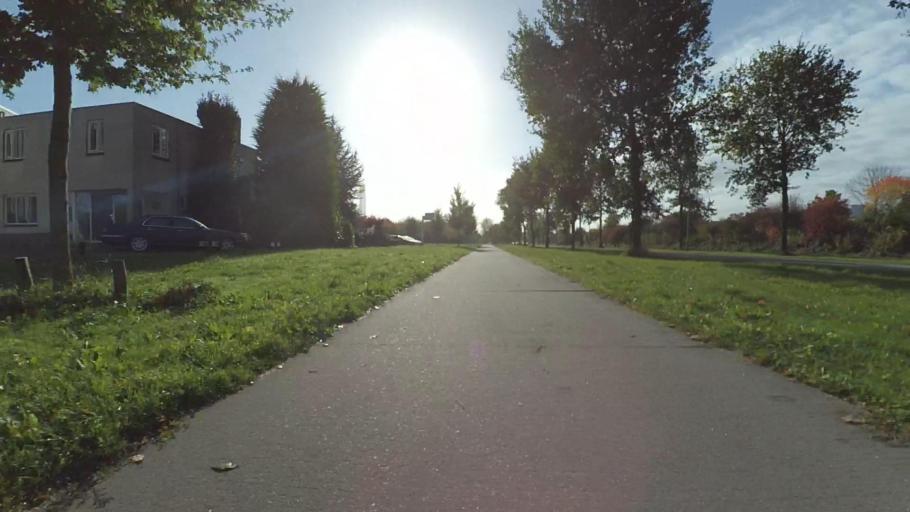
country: NL
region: Flevoland
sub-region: Gemeente Zeewolde
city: Zeewolde
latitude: 52.3369
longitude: 5.5243
